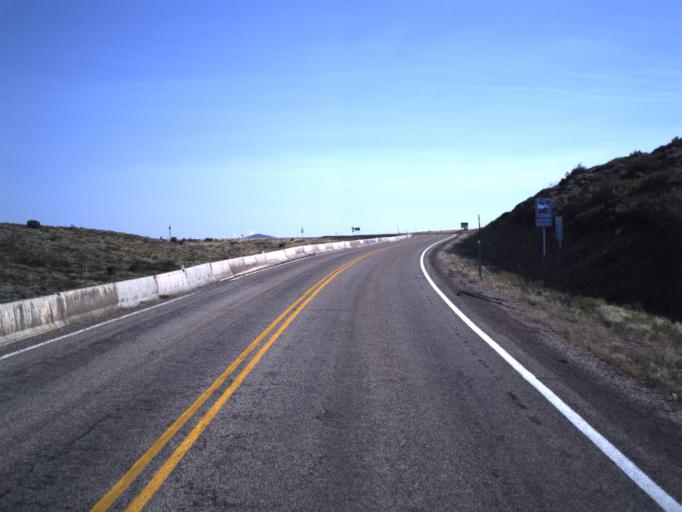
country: US
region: Utah
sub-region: Uintah County
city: Maeser
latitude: 40.6730
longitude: -109.4841
